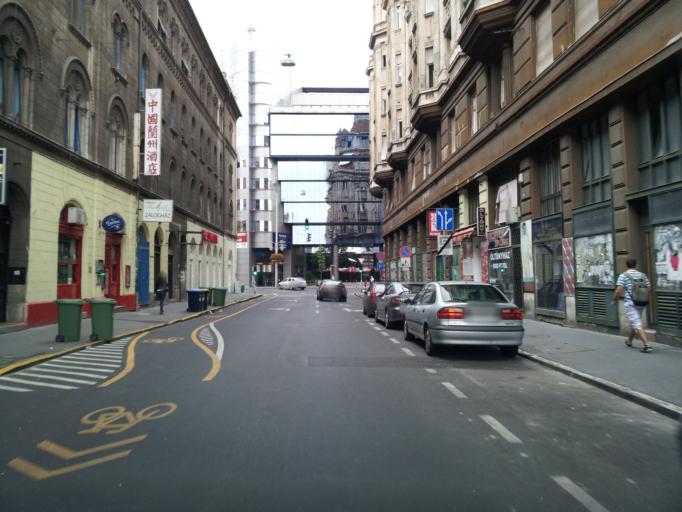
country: HU
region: Budapest
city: Budapest VII. keruelet
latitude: 47.4978
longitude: 19.0757
